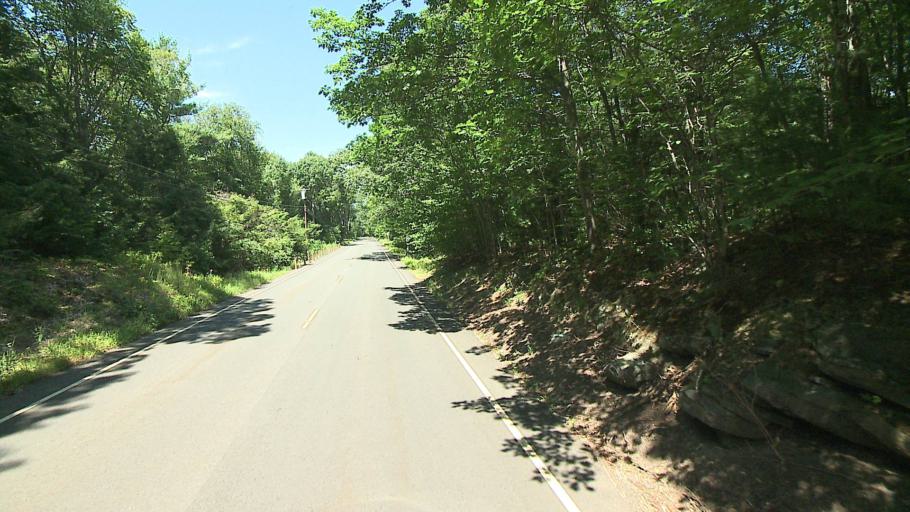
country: US
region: Connecticut
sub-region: Litchfield County
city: Winsted
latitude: 41.9796
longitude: -72.9813
